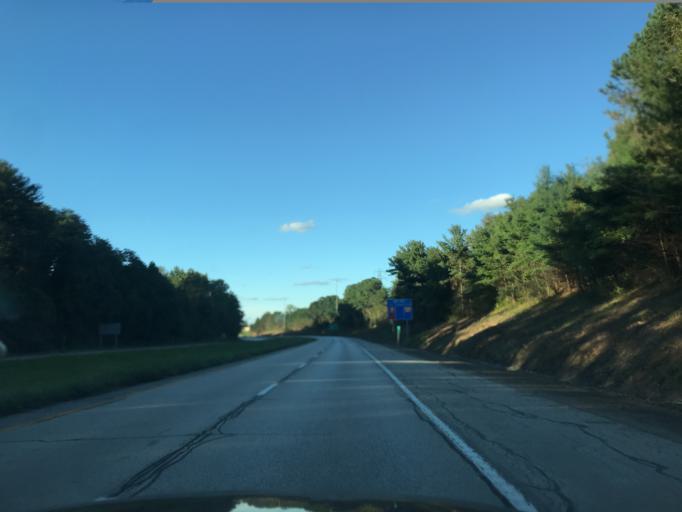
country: US
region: Ohio
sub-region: Ashtabula County
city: Edgewood
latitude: 41.8692
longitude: -80.7614
